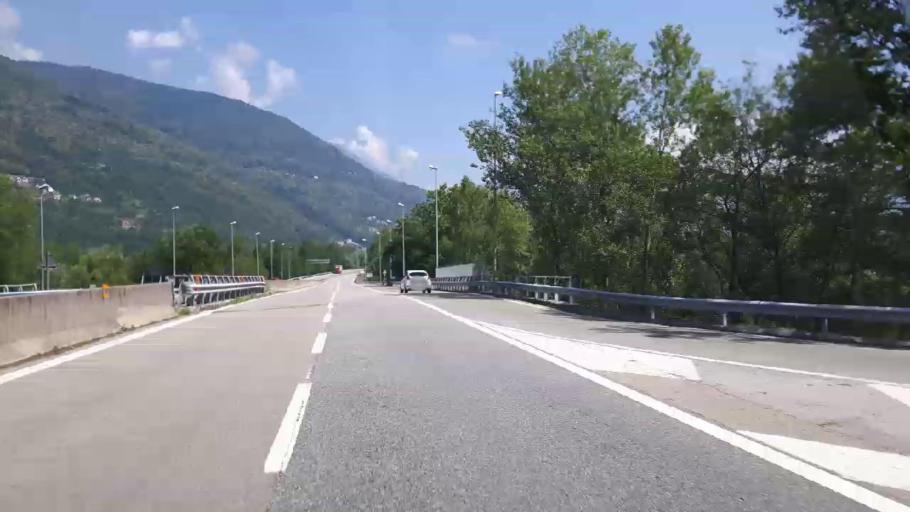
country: IT
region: Piedmont
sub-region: Provincia Verbano-Cusio-Ossola
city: Villadossola
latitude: 46.0723
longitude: 8.2775
